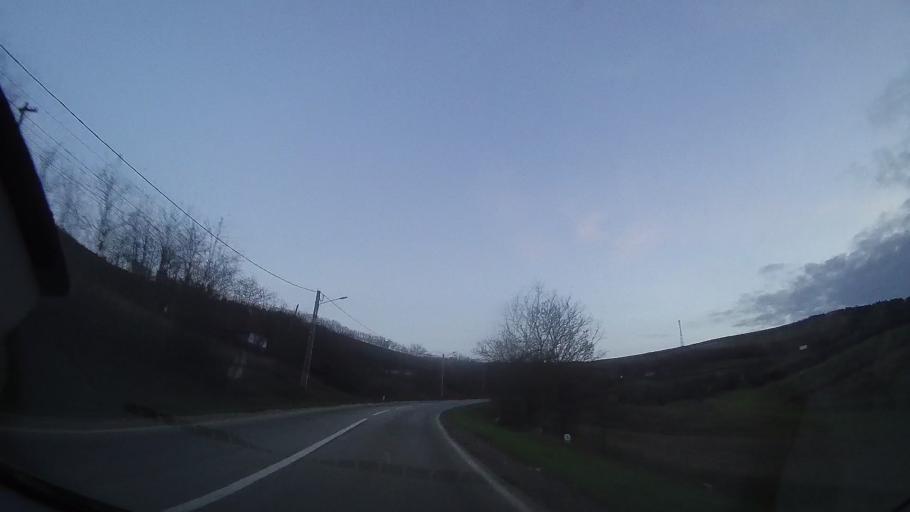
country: RO
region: Cluj
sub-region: Comuna Mociu
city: Mociu
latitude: 46.8045
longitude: 24.0440
